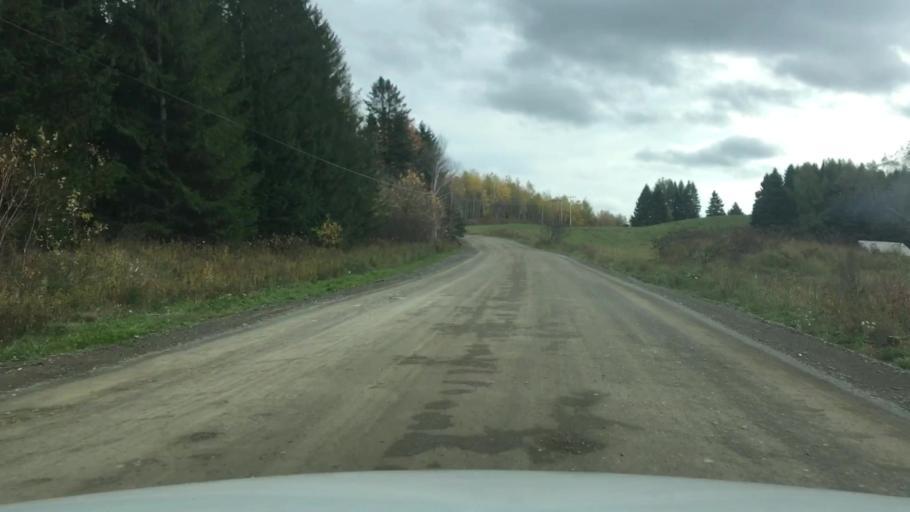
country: US
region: Maine
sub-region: Aroostook County
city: Easton
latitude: 46.5192
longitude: -67.8865
